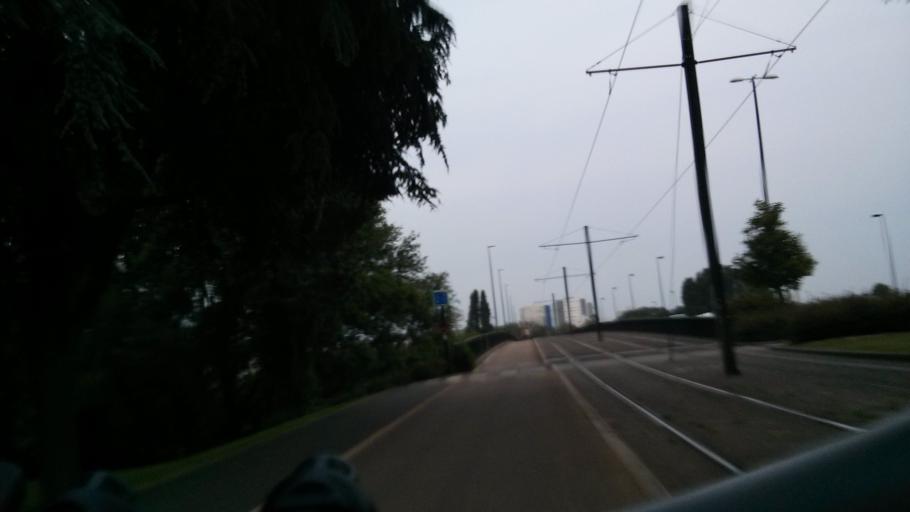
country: FR
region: Pays de la Loire
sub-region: Departement de la Loire-Atlantique
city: Nantes
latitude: 47.2006
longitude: -1.5440
